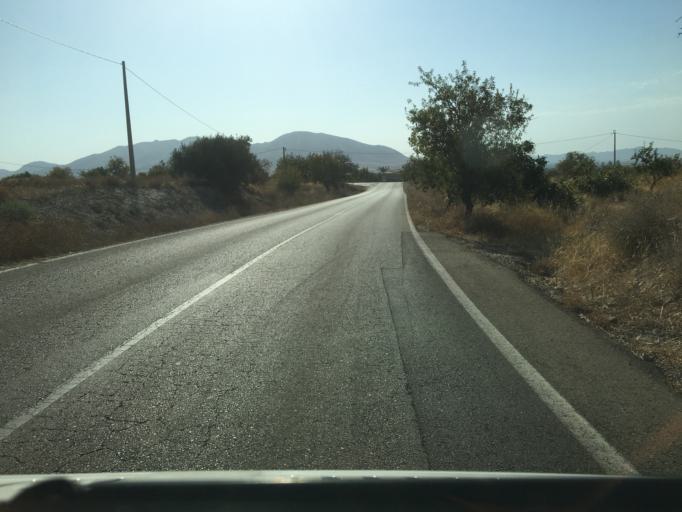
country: ES
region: Andalusia
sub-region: Provincia de Almeria
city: Huercal-Overa
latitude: 37.4704
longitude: -1.9028
